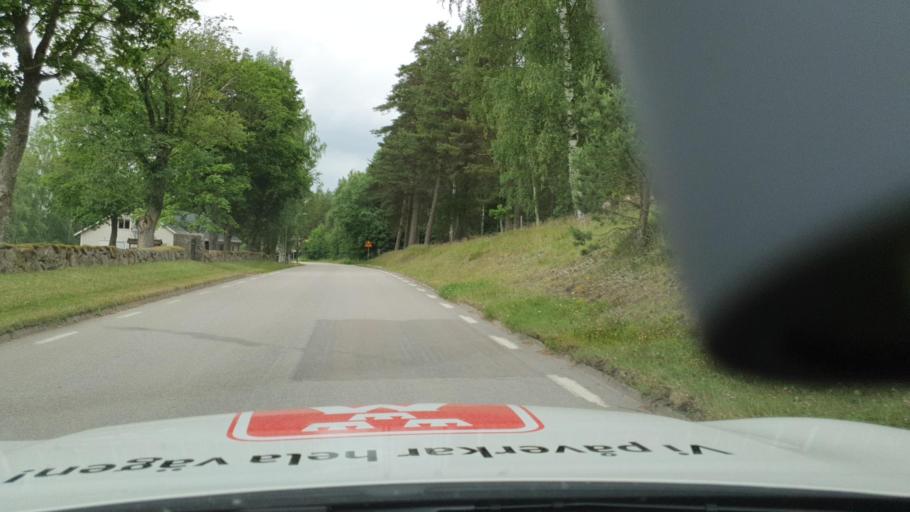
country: SE
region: Vaestra Goetaland
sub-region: Tidaholms Kommun
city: Olofstorp
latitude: 58.2977
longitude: 14.1048
